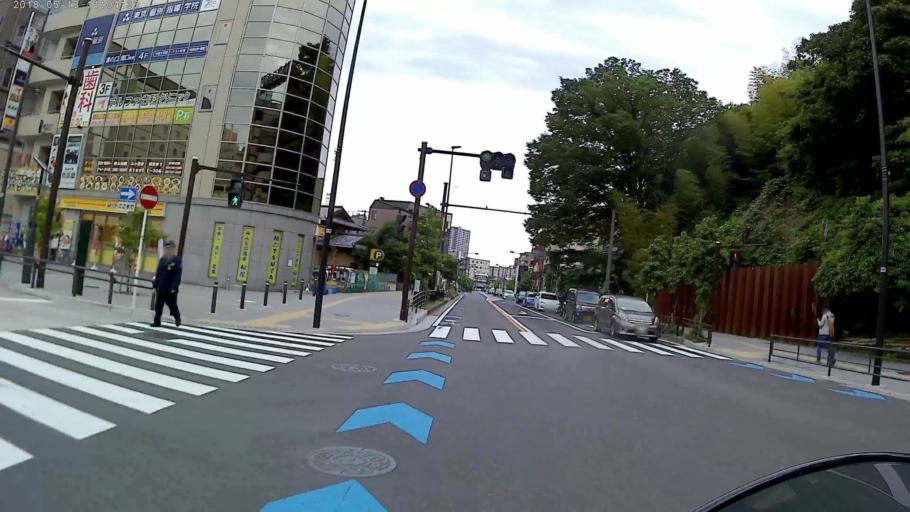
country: JP
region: Tokyo
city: Chofugaoka
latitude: 35.5985
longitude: 139.6104
